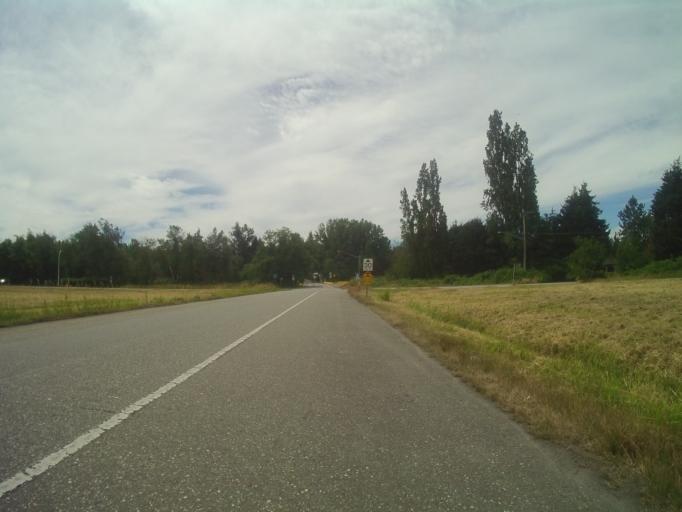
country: CA
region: British Columbia
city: Surrey
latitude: 49.0710
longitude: -122.8245
